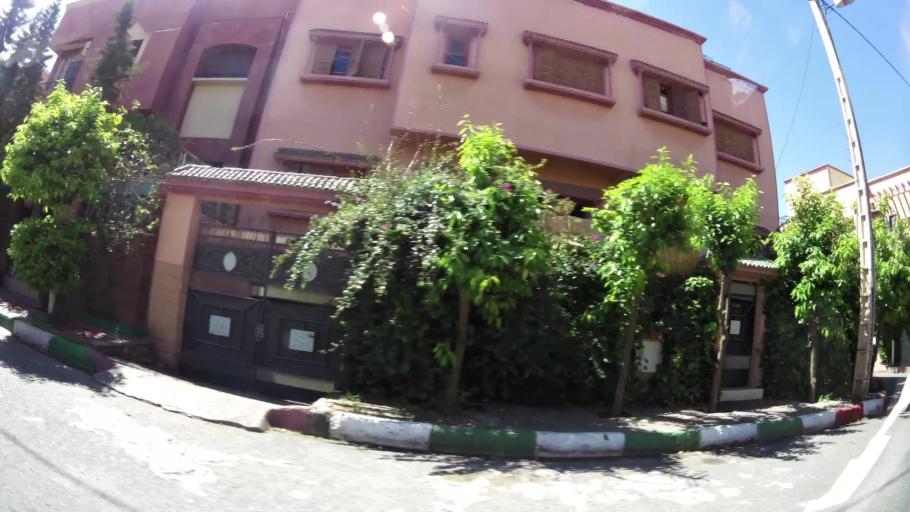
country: MA
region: Marrakech-Tensift-Al Haouz
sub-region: Marrakech
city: Marrakesh
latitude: 31.6380
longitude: -8.0671
